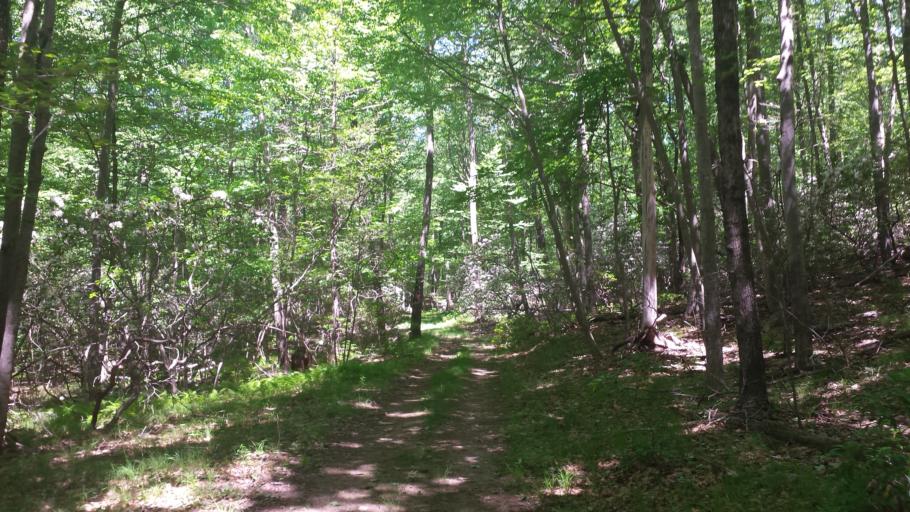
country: US
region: New York
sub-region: Westchester County
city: Pound Ridge
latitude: 41.2373
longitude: -73.5820
